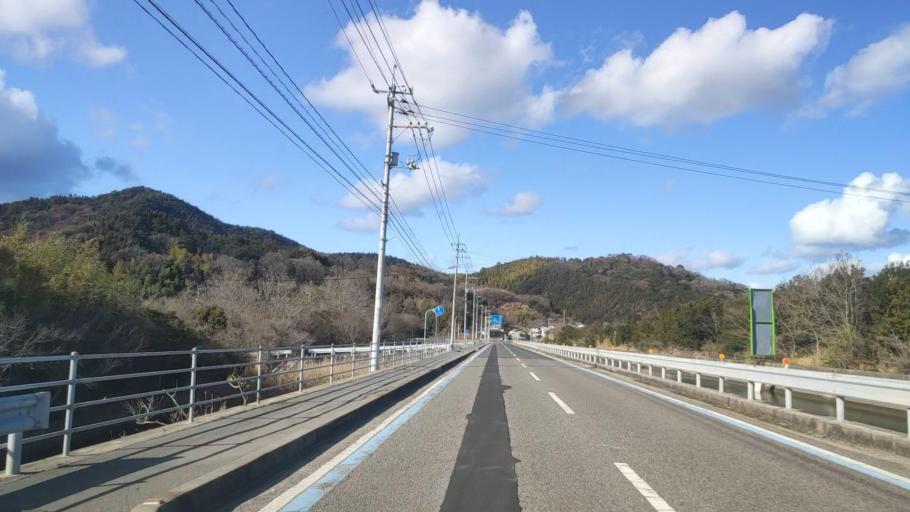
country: JP
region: Hiroshima
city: Innoshima
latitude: 34.2157
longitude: 133.1080
